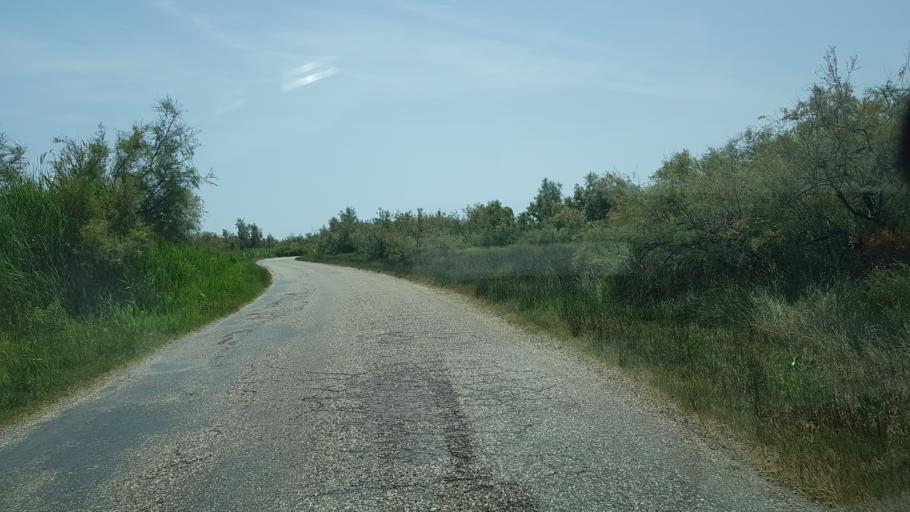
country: FR
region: Provence-Alpes-Cote d'Azur
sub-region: Departement des Bouches-du-Rhone
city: Arles
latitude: 43.5381
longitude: 4.6406
